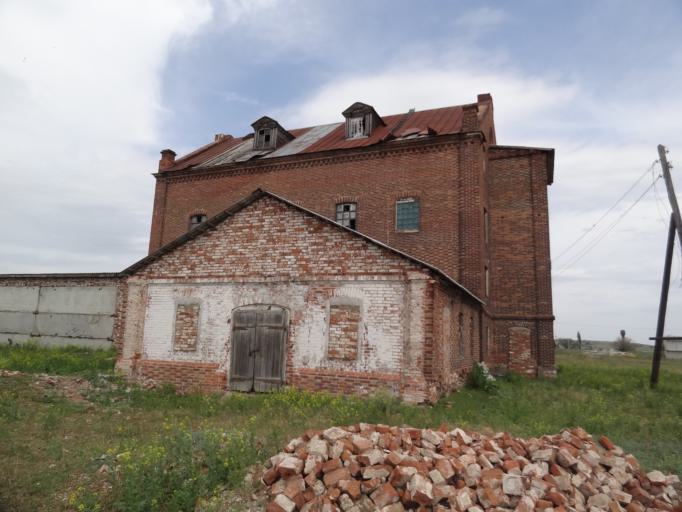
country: RU
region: Saratov
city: Privolzhskiy
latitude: 51.1985
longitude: 45.9081
